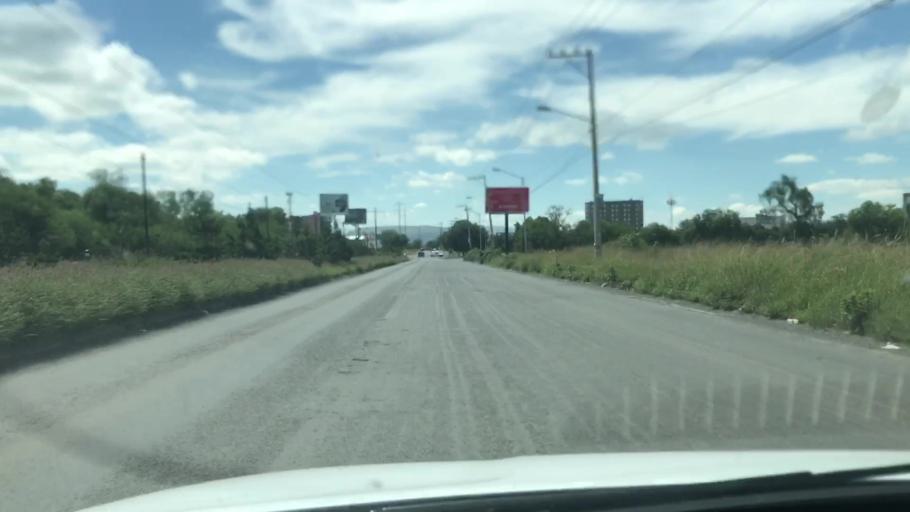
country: MX
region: Guanajuato
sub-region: Celaya
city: La Trinidad
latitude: 20.5388
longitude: -100.7787
